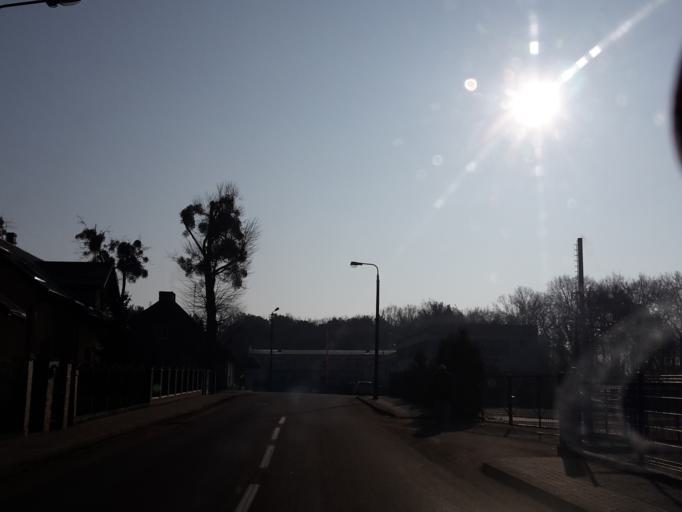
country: PL
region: Kujawsko-Pomorskie
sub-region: Powiat brodnicki
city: Brodnica
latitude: 53.2613
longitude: 19.4089
